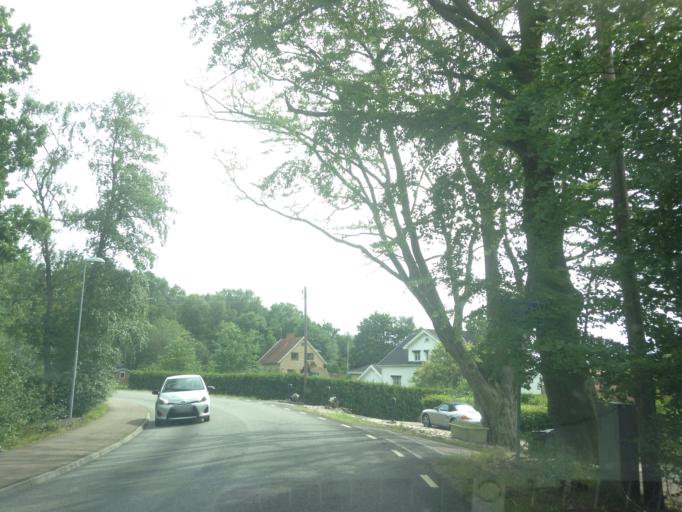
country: SE
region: Vaestra Goetaland
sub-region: Goteborg
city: Goeteborg
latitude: 57.7754
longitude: 11.9526
